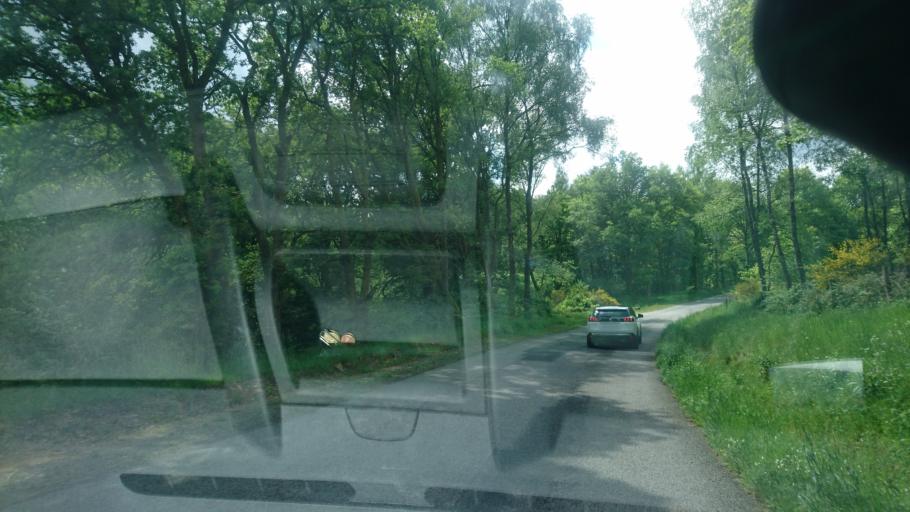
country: FR
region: Limousin
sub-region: Departement de la Haute-Vienne
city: Peyrat-le-Chateau
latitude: 45.7867
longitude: 1.9012
